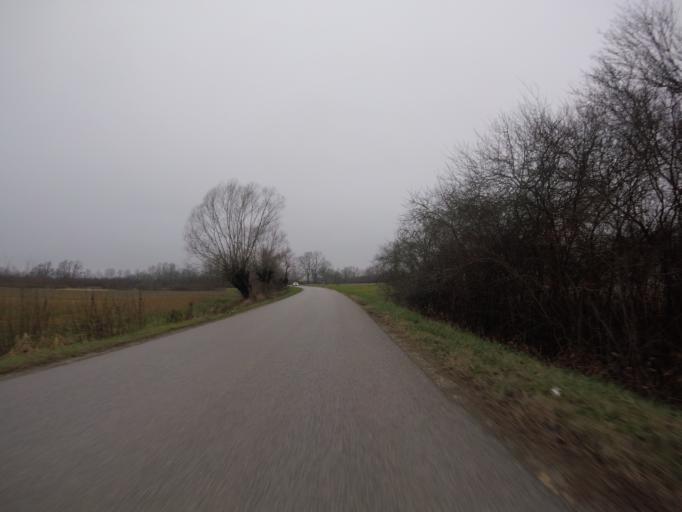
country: HR
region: Sisacko-Moslavacka
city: Lekenik
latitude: 45.6300
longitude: 16.3109
